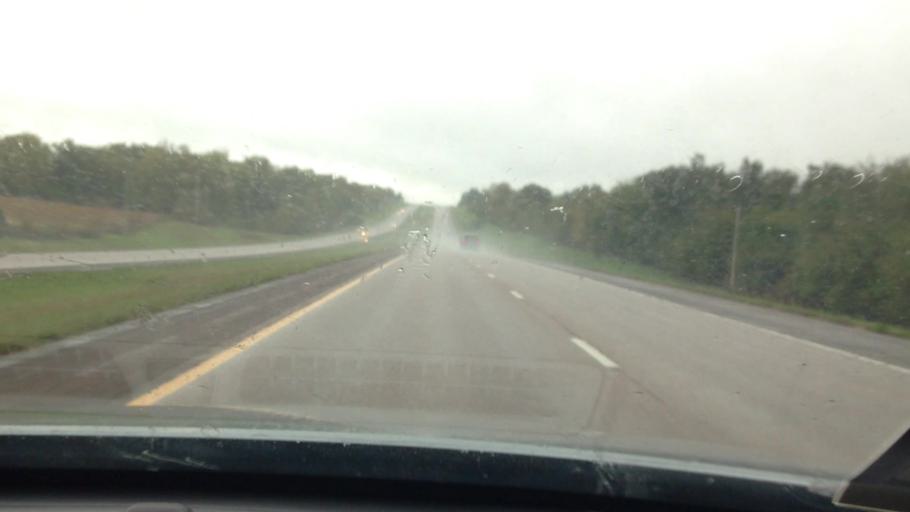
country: US
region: Kansas
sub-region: Leavenworth County
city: Lansing
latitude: 39.1955
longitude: -94.9002
